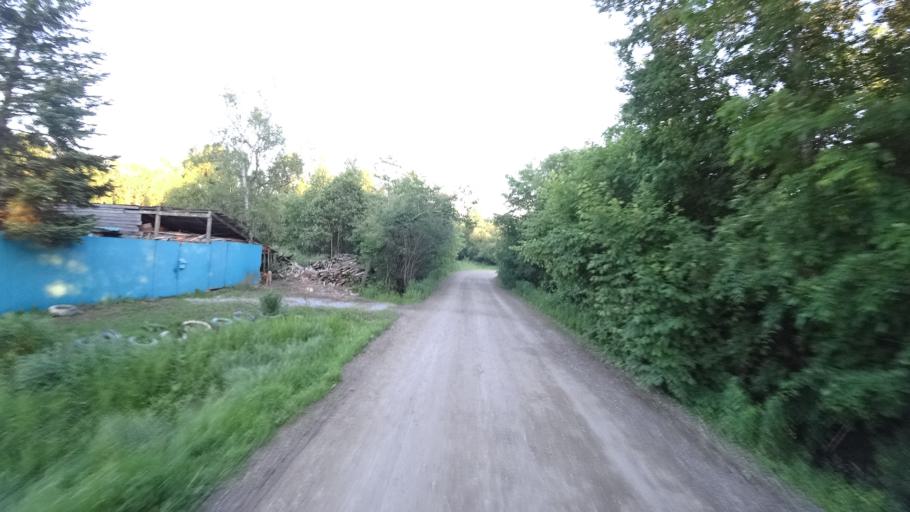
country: RU
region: Khabarovsk Krai
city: Khor
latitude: 47.8504
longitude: 134.9838
